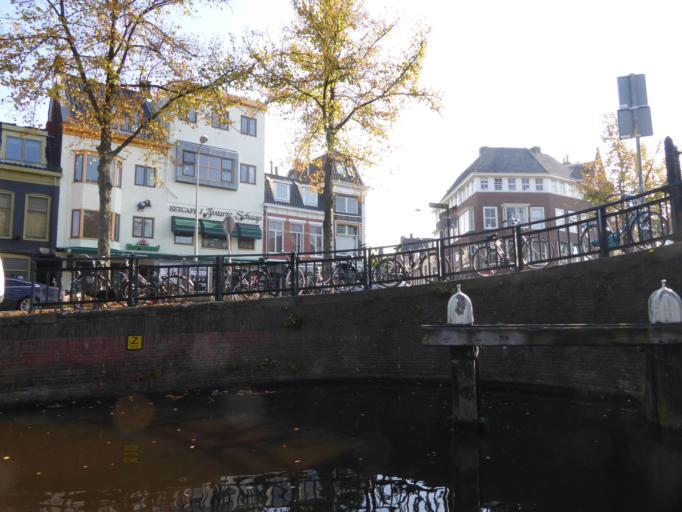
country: NL
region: Groningen
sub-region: Gemeente Groningen
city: Groningen
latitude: 53.2187
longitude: 6.5727
